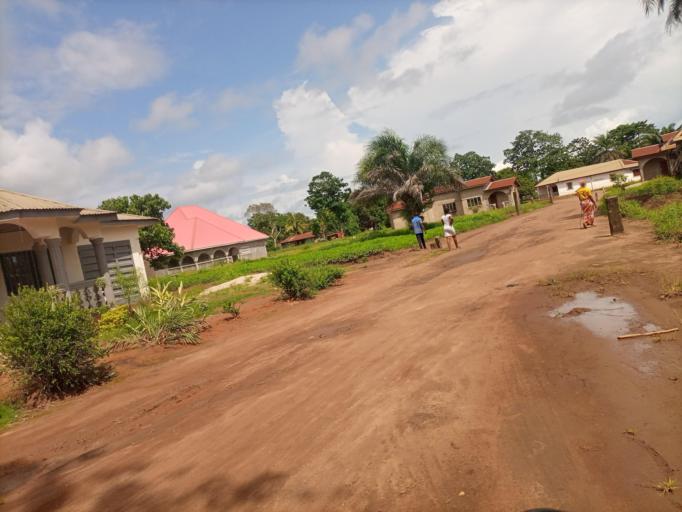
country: SL
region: Northern Province
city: Tintafor
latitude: 8.6389
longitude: -13.2140
